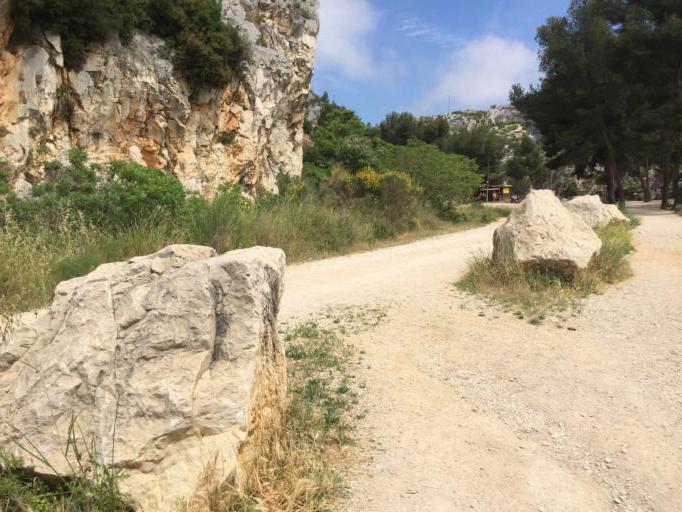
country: FR
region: Provence-Alpes-Cote d'Azur
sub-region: Departement des Bouches-du-Rhone
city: Cassis
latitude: 43.2117
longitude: 5.5212
